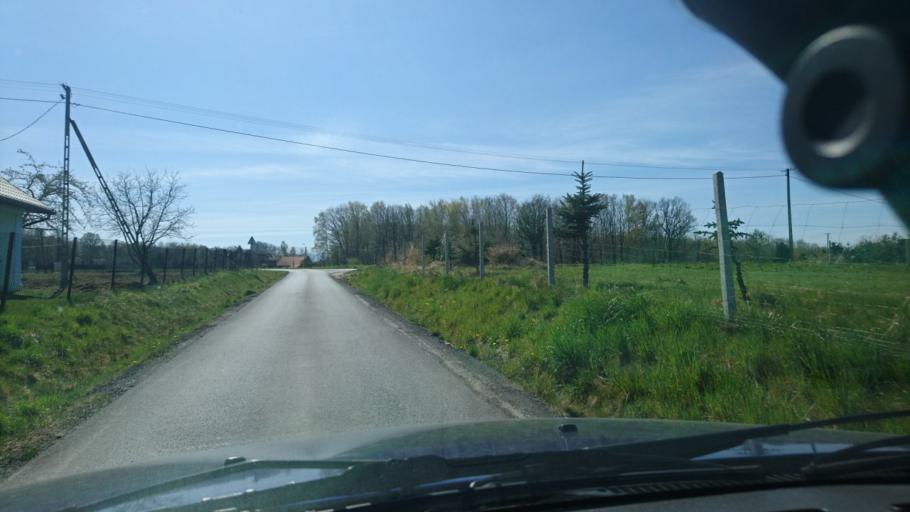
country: PL
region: Silesian Voivodeship
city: Janowice
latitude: 49.8889
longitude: 19.1031
